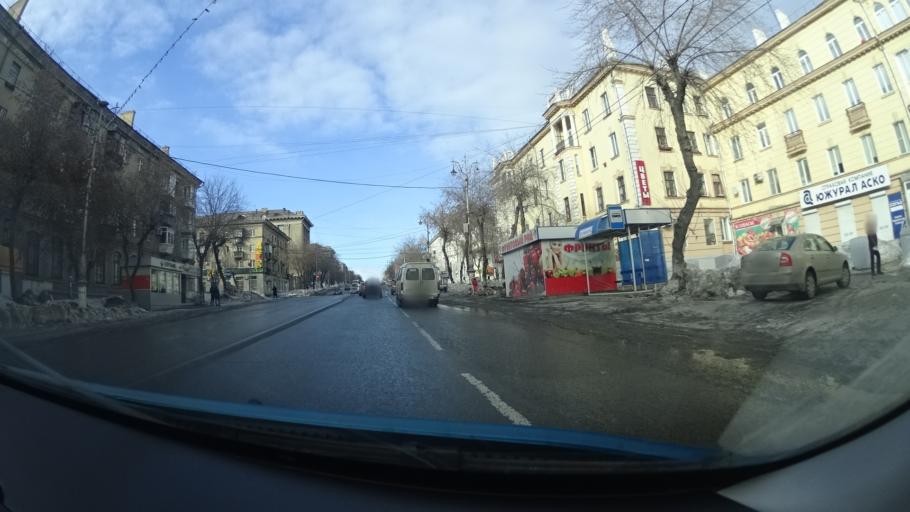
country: RU
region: Chelyabinsk
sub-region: Gorod Magnitogorsk
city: Magnitogorsk
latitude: 53.4254
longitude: 58.9837
